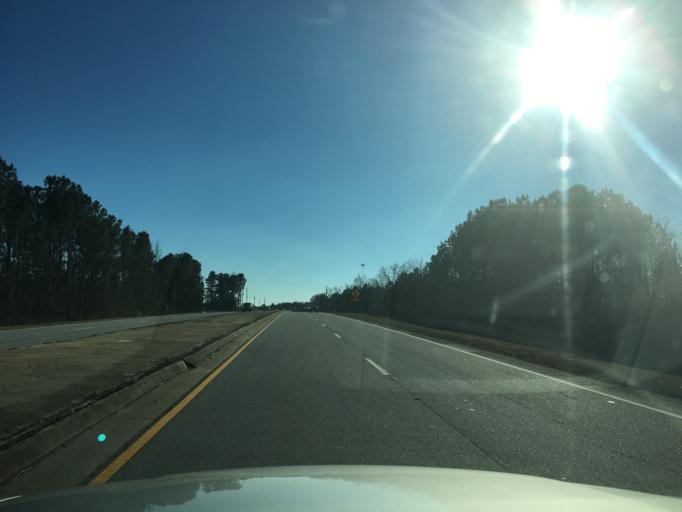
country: US
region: Georgia
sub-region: Carroll County
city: Carrollton
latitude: 33.5179
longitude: -85.0768
